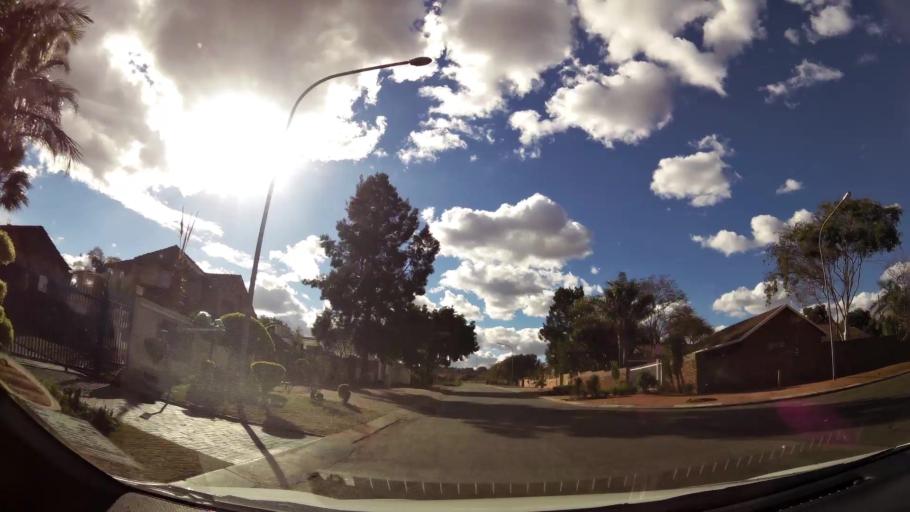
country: ZA
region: Limpopo
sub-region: Capricorn District Municipality
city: Polokwane
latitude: -23.9027
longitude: 29.4951
